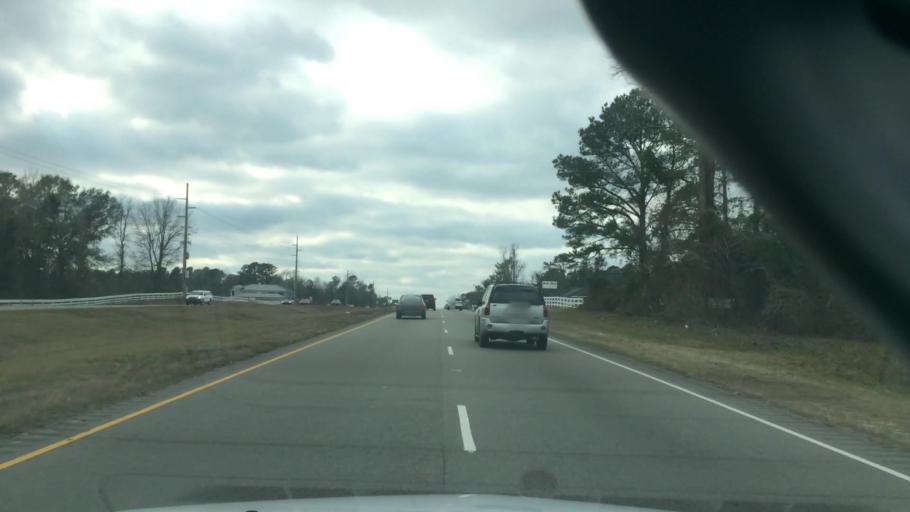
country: US
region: North Carolina
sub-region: Brunswick County
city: Shallotte
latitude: 34.0120
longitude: -78.2893
